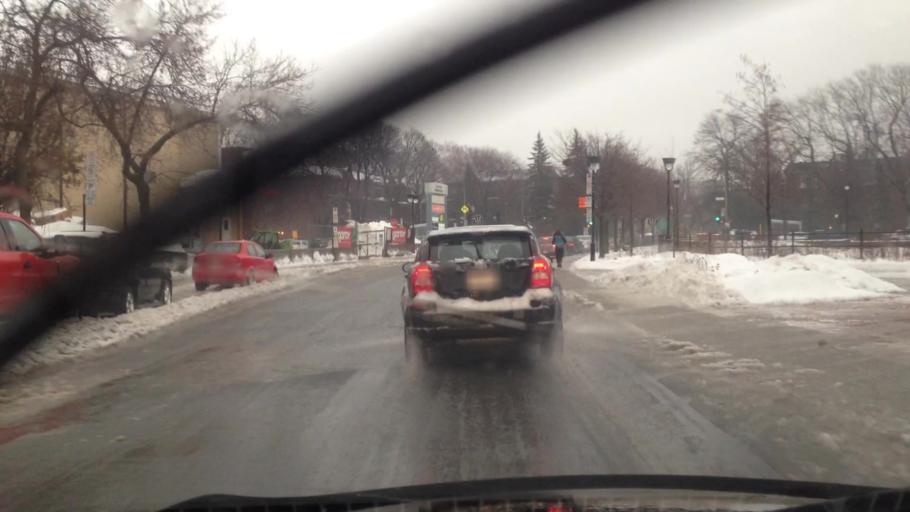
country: CA
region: Quebec
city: Mont-Royal
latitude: 45.5081
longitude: -73.6268
